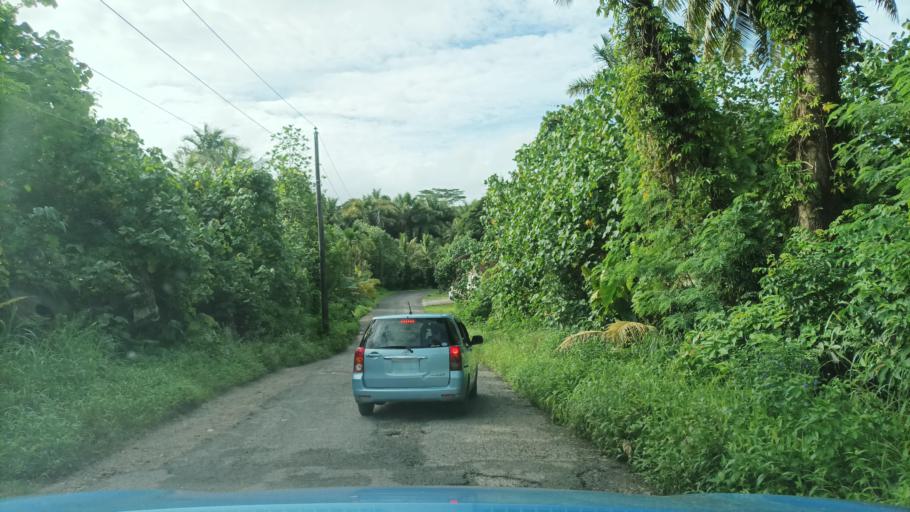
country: FM
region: Pohnpei
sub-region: Kolonia Municipality
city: Kolonia
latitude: 6.9511
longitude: 158.2264
